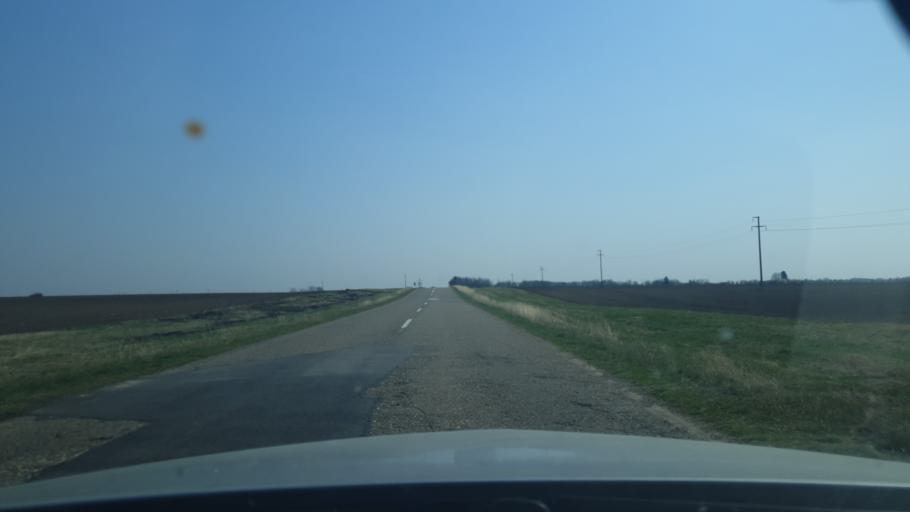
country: RS
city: Sasinci
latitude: 45.0262
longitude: 19.7595
